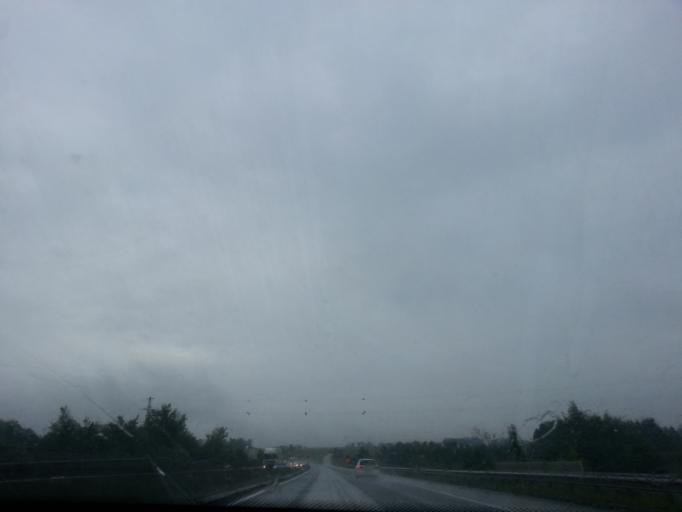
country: AT
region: Upper Austria
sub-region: Wels-Land
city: Sattledt
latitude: 48.0093
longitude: 14.0718
